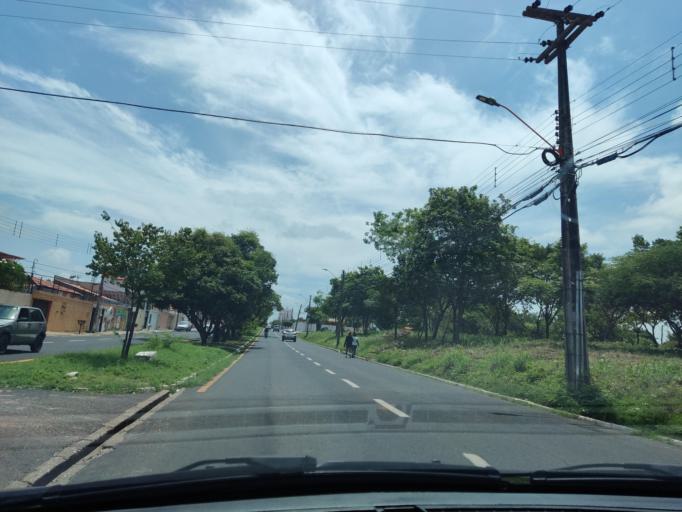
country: BR
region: Piaui
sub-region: Teresina
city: Teresina
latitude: -5.0702
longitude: -42.7550
